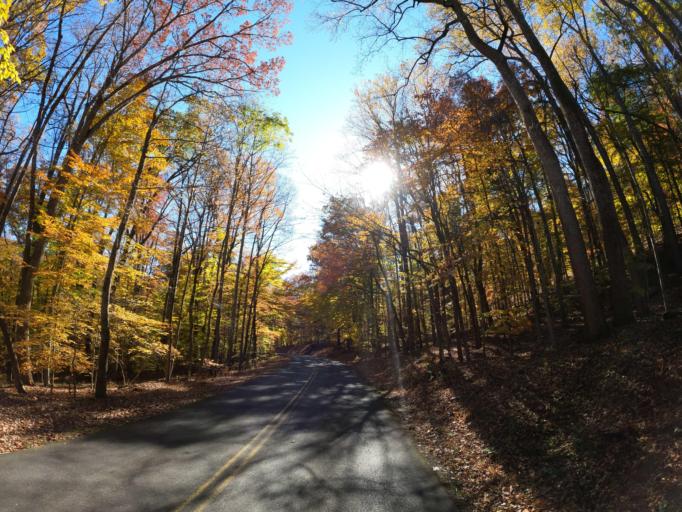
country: US
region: Maryland
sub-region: Frederick County
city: Thurmont
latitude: 39.6226
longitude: -77.4664
